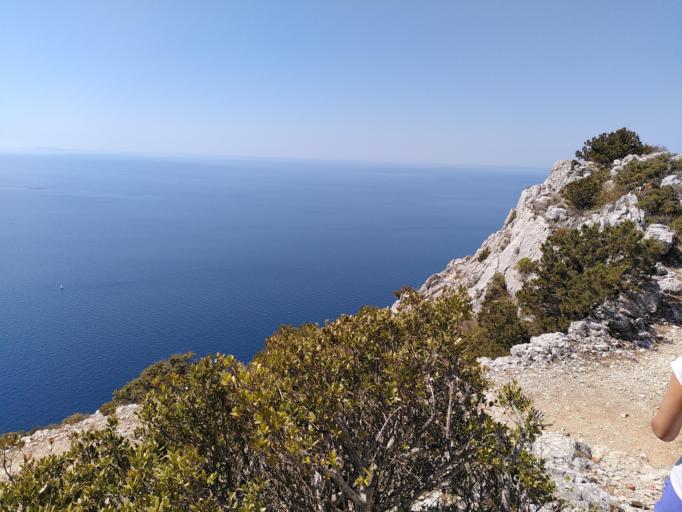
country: HR
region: Splitsko-Dalmatinska
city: Stari Grad
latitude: 43.1459
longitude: 16.5823
